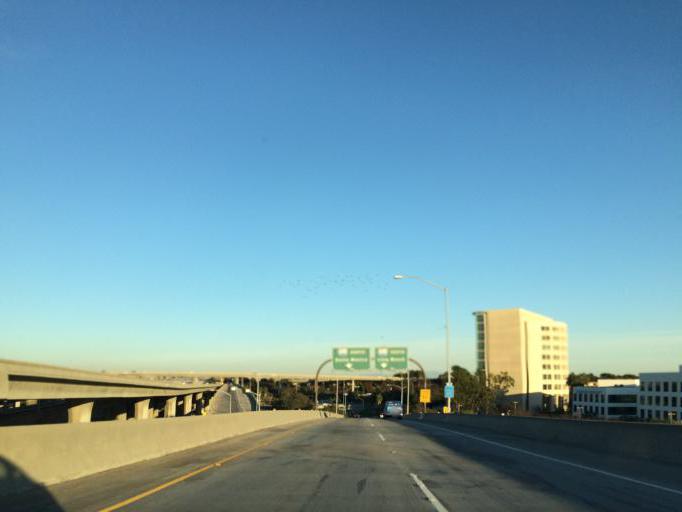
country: US
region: California
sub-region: Los Angeles County
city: Del Aire
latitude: 33.9297
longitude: -118.3753
